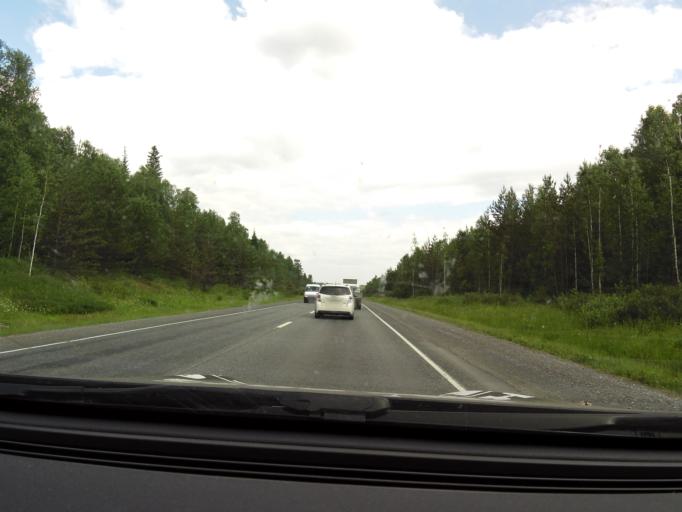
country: RU
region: Sverdlovsk
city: Nizhniye Sergi
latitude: 56.8249
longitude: 59.2483
